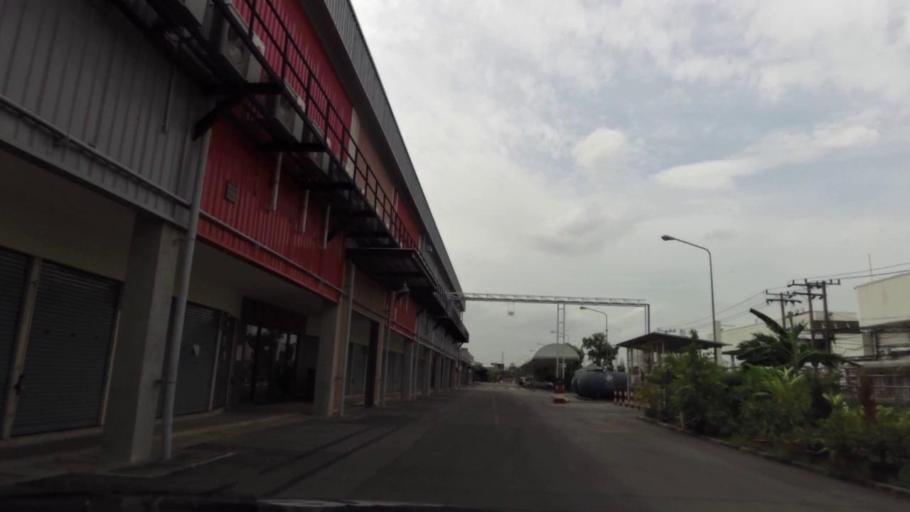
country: TH
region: Bangkok
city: Bang Kapi
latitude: 13.7658
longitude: 100.6397
